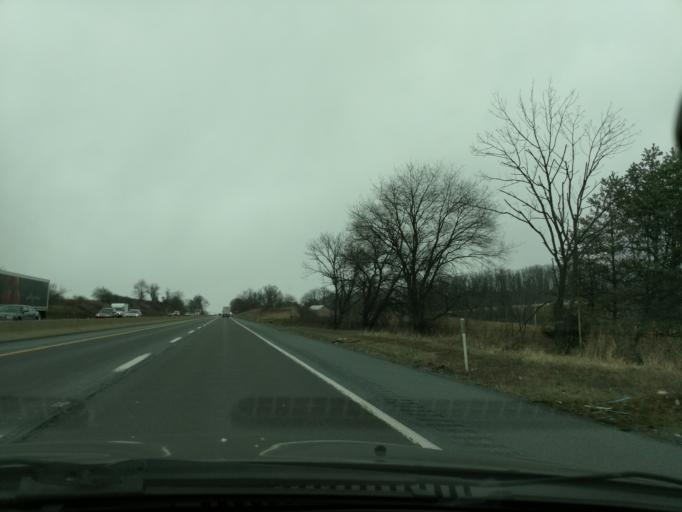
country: US
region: Pennsylvania
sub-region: Berks County
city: West Hamburg
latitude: 40.5368
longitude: -76.0520
